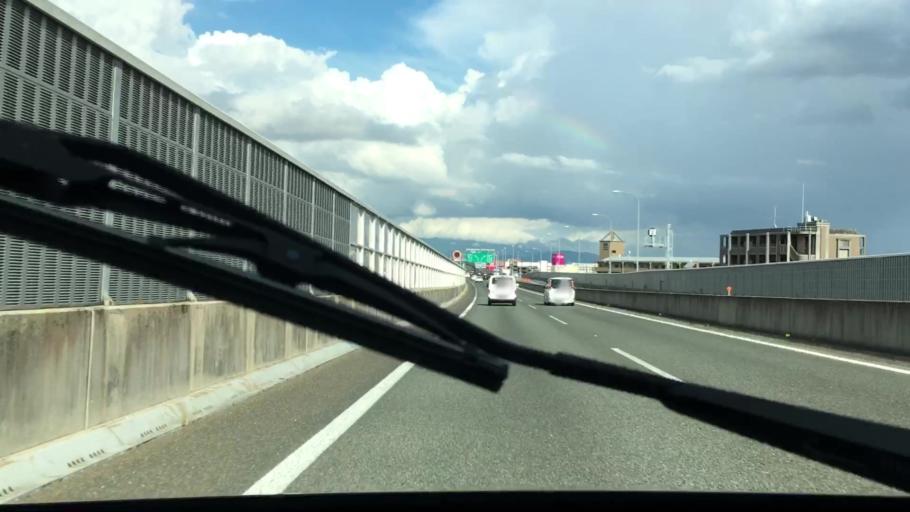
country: JP
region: Fukuoka
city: Maebaru-chuo
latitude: 33.5692
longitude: 130.3057
